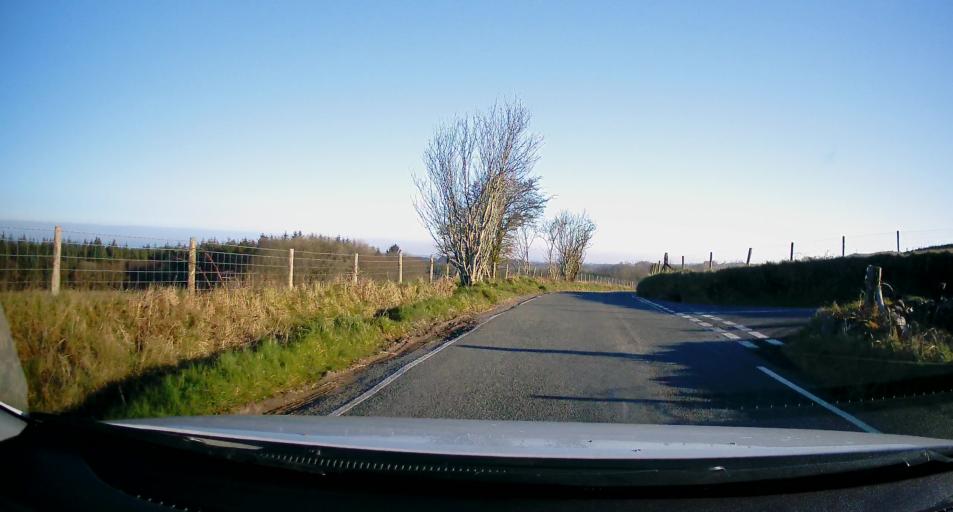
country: GB
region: Wales
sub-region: County of Ceredigion
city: Lledrod
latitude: 52.2605
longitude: -4.0748
